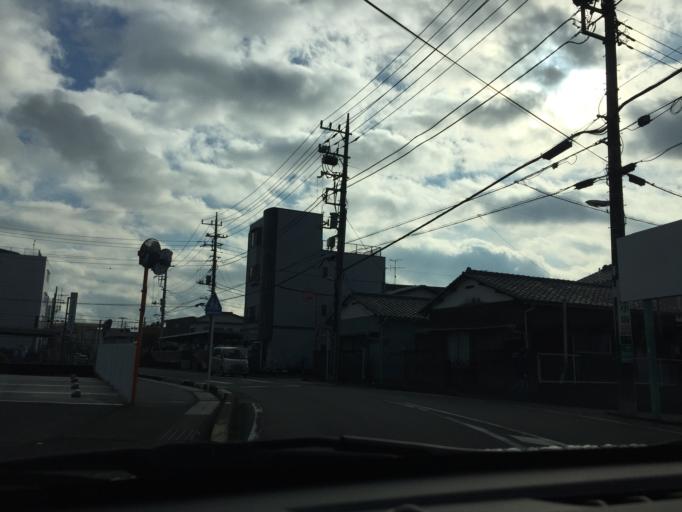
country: JP
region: Shizuoka
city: Mishima
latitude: 35.1377
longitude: 138.8957
